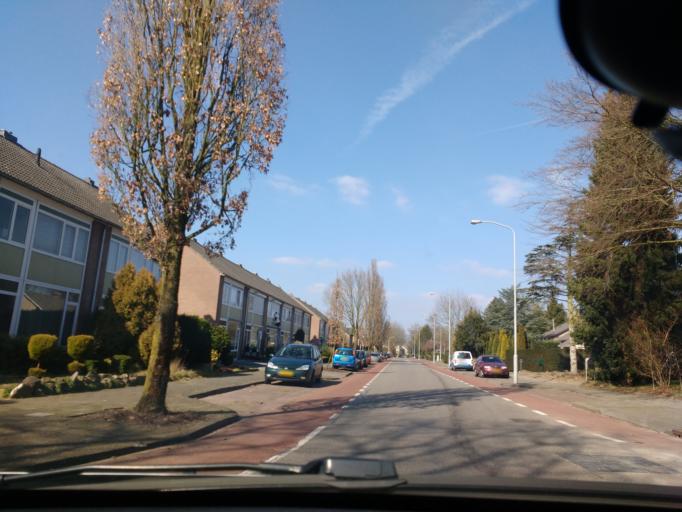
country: NL
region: North Brabant
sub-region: Gemeente Cuijk
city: Cuijk
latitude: 51.7848
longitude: 5.8589
